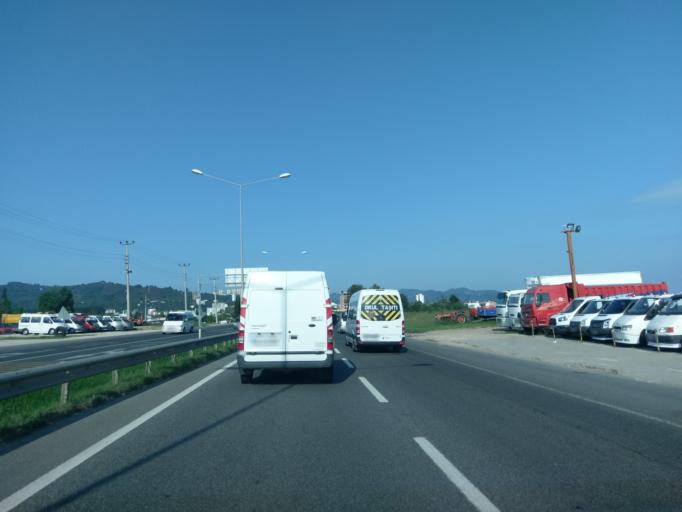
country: TR
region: Ordu
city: Fatsa
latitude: 41.0211
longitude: 37.5352
